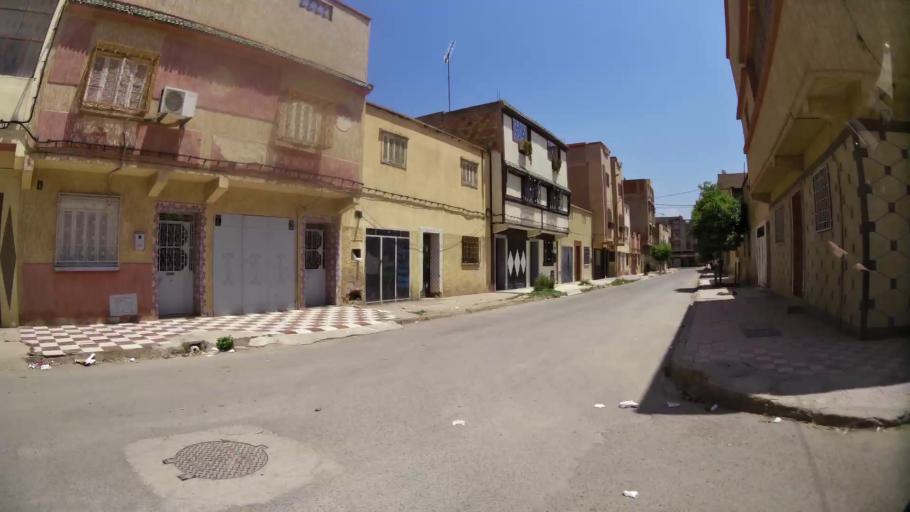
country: MA
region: Oriental
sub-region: Oujda-Angad
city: Oujda
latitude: 34.7005
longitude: -1.8948
